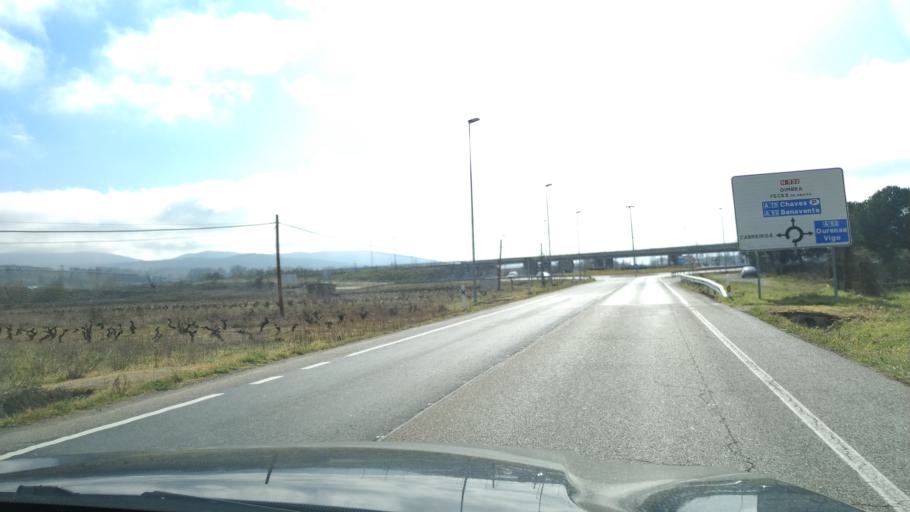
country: ES
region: Galicia
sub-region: Provincia de Ourense
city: Verin
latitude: 41.9149
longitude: -7.4433
